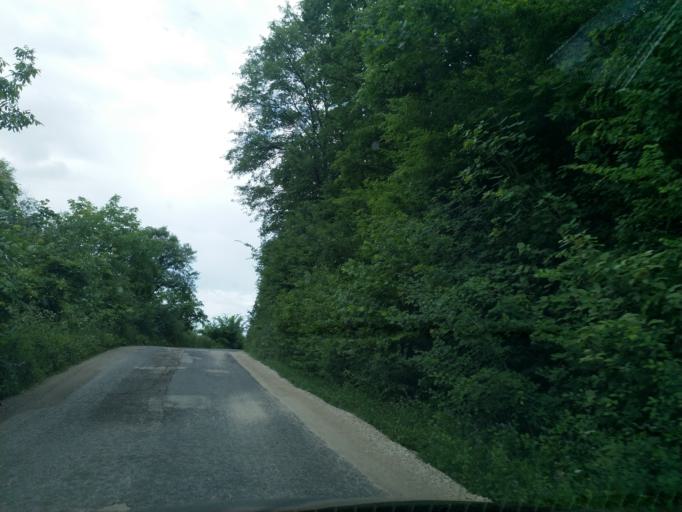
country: RS
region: Central Serbia
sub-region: Borski Okrug
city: Bor
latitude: 44.0240
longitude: 21.9778
